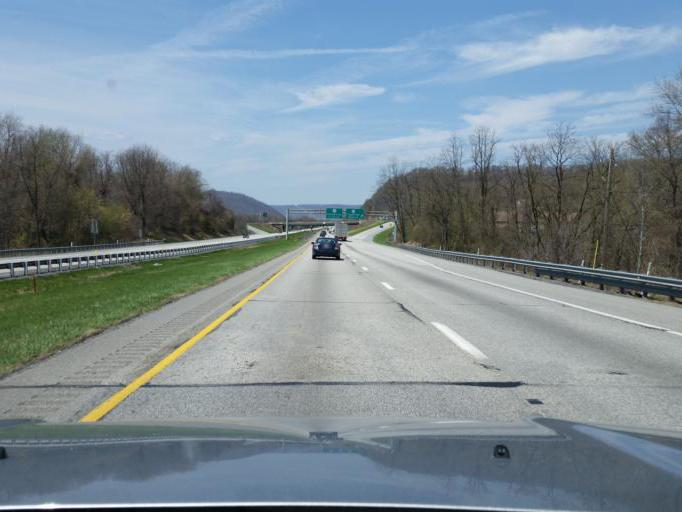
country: US
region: Pennsylvania
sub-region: Dauphin County
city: Harrisburg
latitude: 40.3221
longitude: -76.8854
